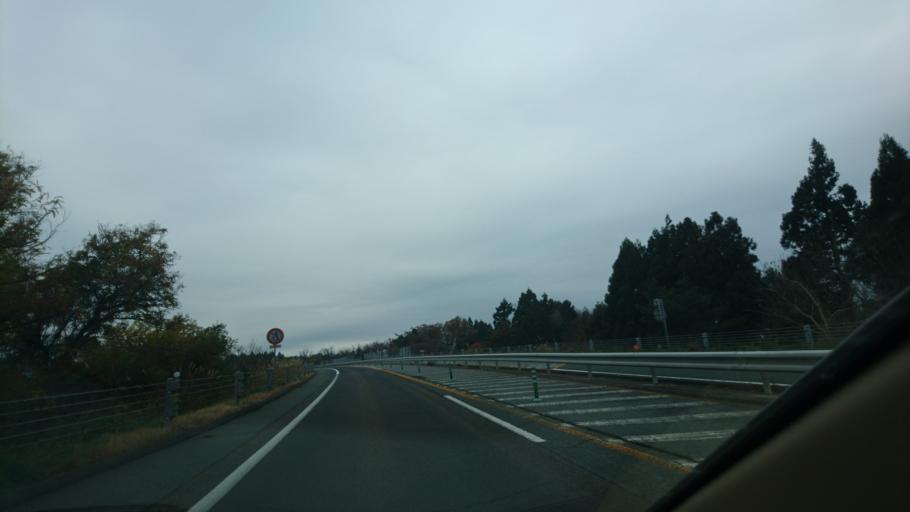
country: JP
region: Iwate
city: Kitakami
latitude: 39.2792
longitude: 141.0634
